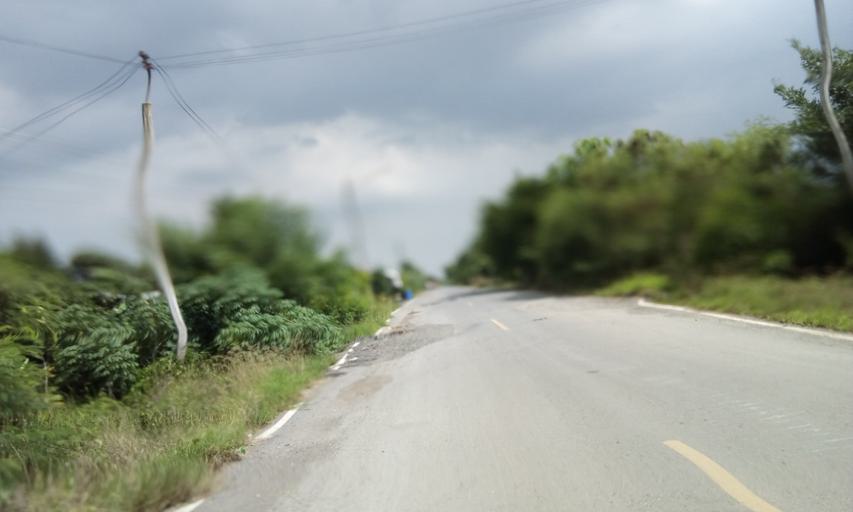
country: TH
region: Pathum Thani
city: Ban Lam Luk Ka
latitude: 14.0307
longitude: 100.8474
